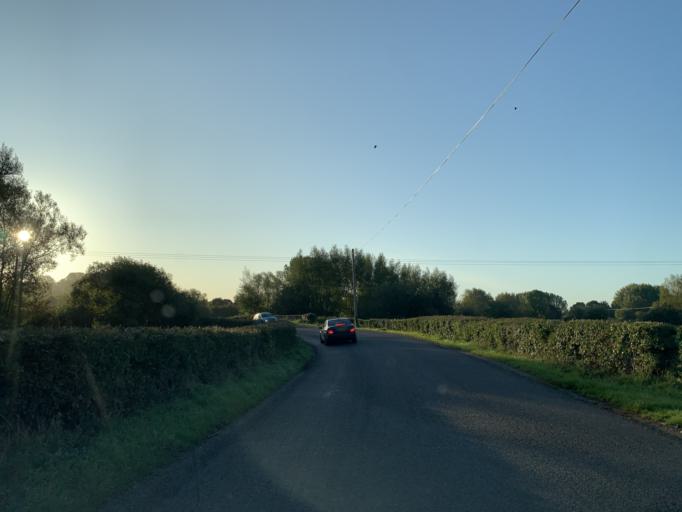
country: GB
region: England
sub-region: Wiltshire
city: Woodford
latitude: 51.0964
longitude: -1.8193
